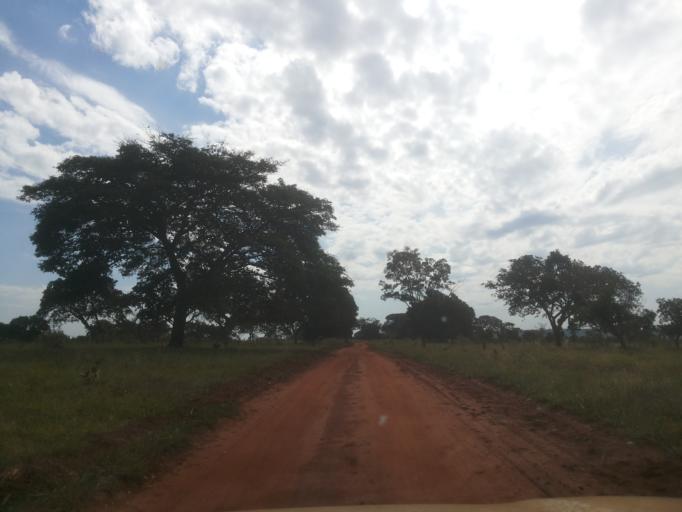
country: BR
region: Minas Gerais
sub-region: Ituiutaba
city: Ituiutaba
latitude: -19.0648
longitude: -49.3644
